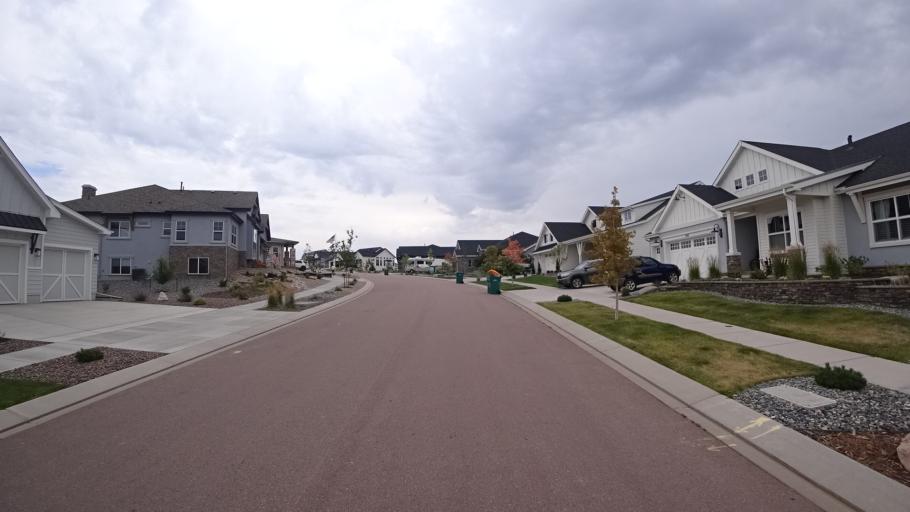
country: US
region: Colorado
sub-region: El Paso County
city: Gleneagle
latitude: 39.0034
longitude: -104.8090
